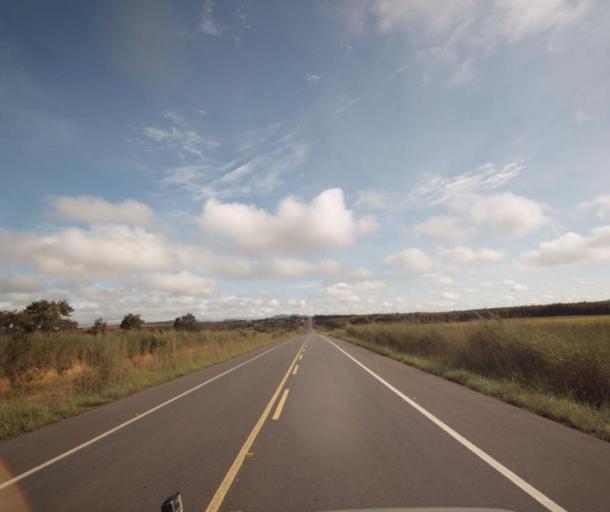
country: BR
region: Goias
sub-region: Barro Alto
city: Barro Alto
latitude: -15.2239
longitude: -48.6957
